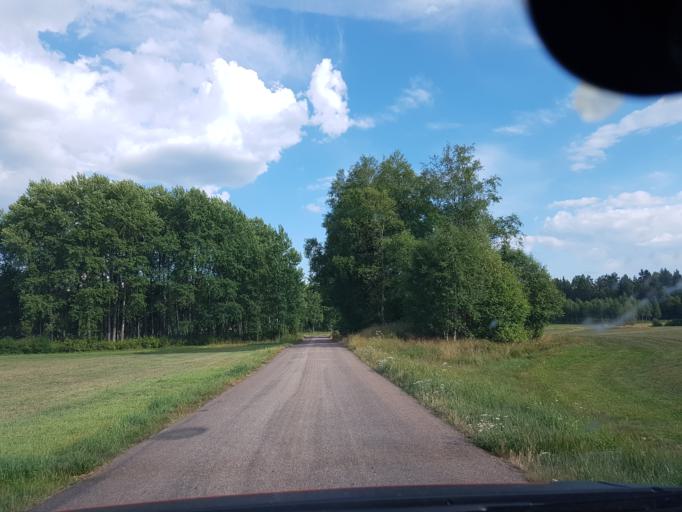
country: SE
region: Joenkoeping
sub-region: Gislaveds Kommun
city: Reftele
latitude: 57.2043
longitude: 13.5969
